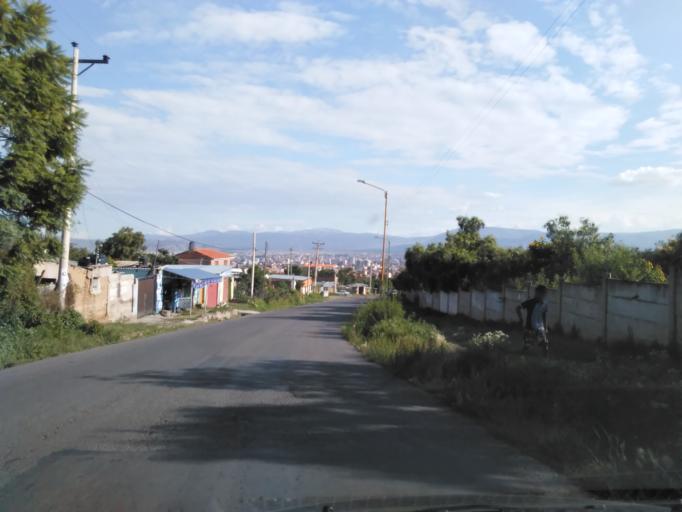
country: BO
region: Cochabamba
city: Cochabamba
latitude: -17.3417
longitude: -66.1834
